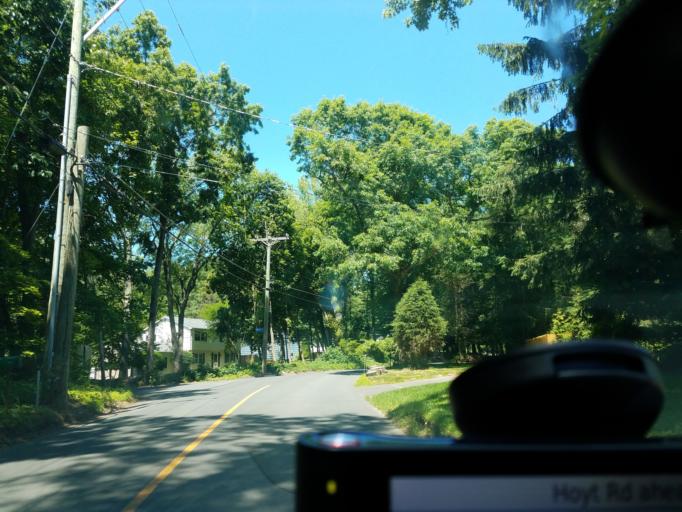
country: US
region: Connecticut
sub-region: Fairfield County
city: Bethel
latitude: 41.3936
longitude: -73.3883
